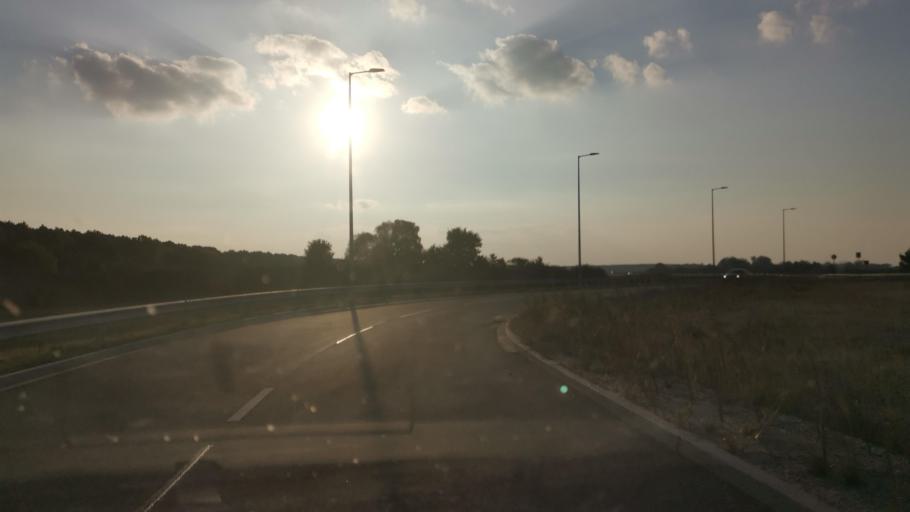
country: HU
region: Gyor-Moson-Sopron
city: Mihalyi
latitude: 47.5622
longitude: 17.0855
